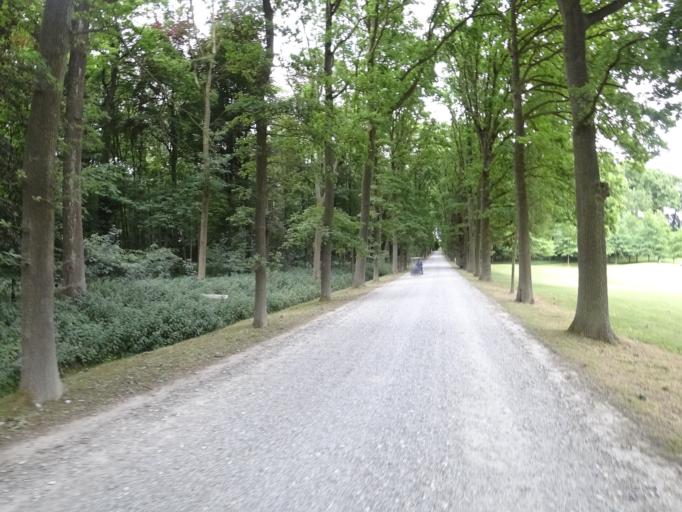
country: BE
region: Wallonia
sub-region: Province du Hainaut
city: Enghien
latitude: 50.6875
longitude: 4.0514
